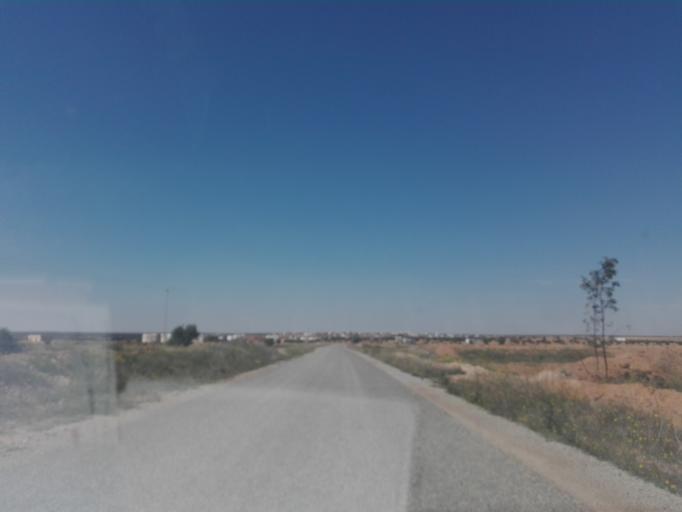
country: TN
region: Safaqis
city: Bi'r `Ali Bin Khalifah
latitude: 34.6720
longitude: 10.3735
